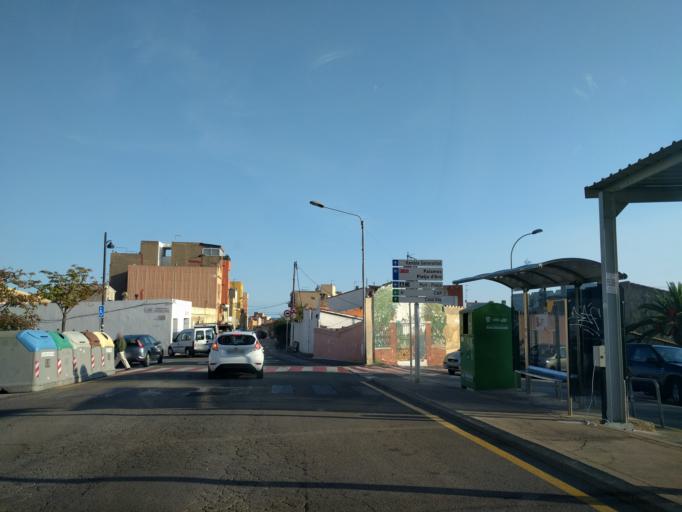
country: ES
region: Catalonia
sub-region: Provincia de Girona
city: Sant Feliu de Guixols
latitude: 41.7874
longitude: 3.0285
